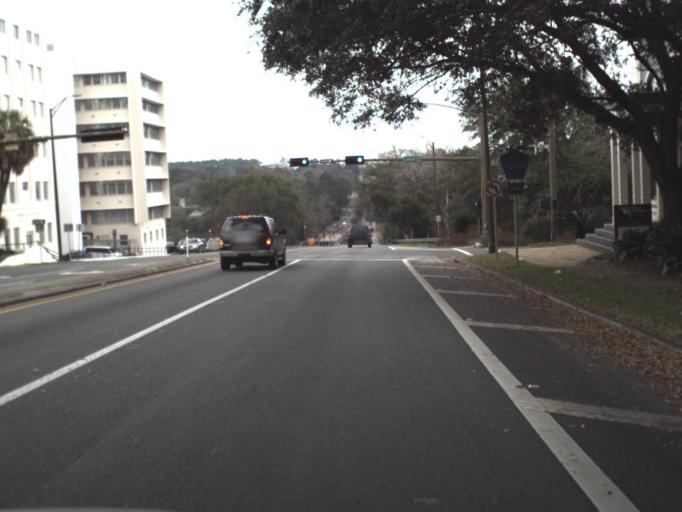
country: US
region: Florida
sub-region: Leon County
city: Tallahassee
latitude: 30.4380
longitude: -84.2802
